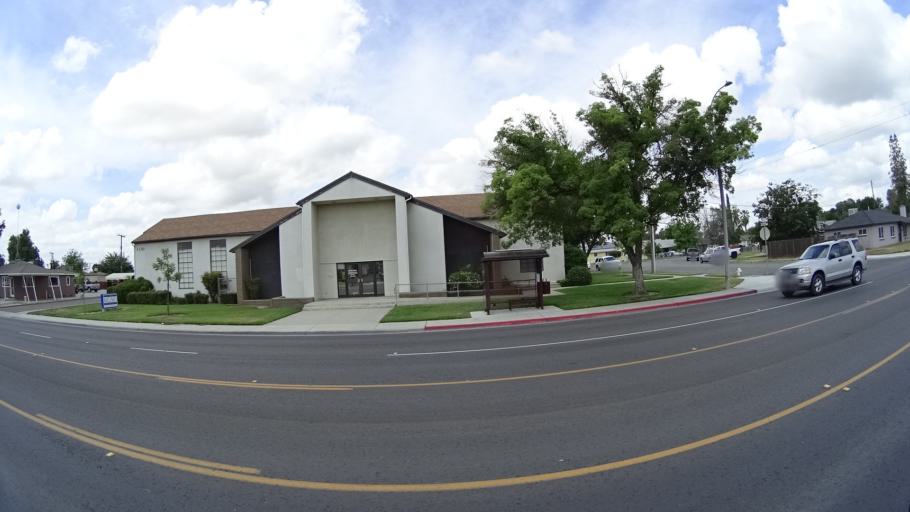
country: US
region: California
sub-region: Kings County
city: Hanford
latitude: 36.3364
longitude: -119.6551
